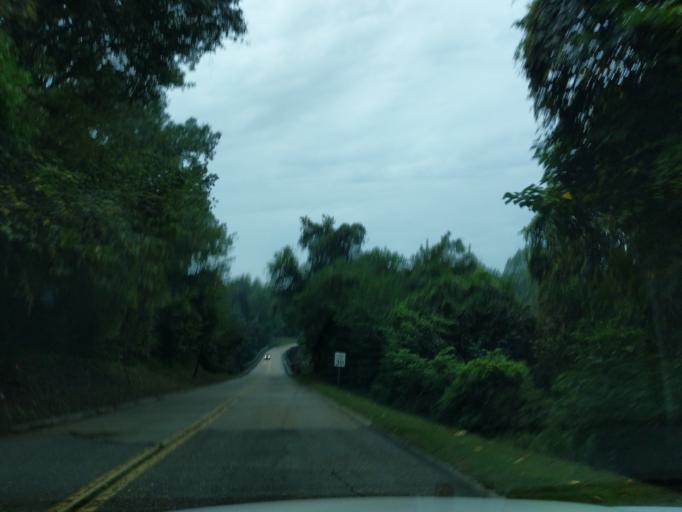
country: US
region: Mississippi
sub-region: Warren County
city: Vicksburg
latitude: 32.3181
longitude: -90.8916
